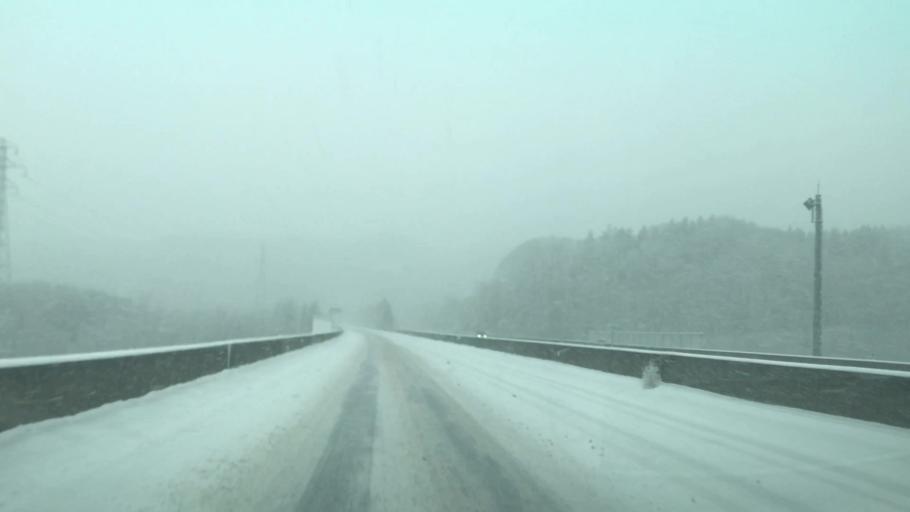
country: JP
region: Hokkaido
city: Muroran
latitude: 42.4276
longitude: 141.0964
